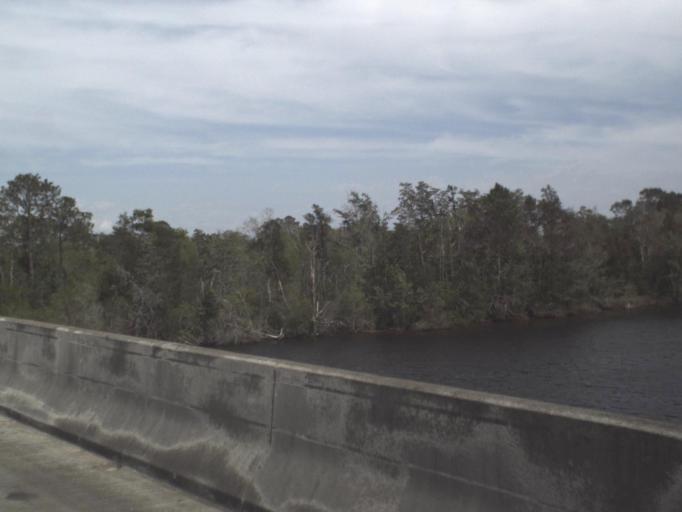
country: US
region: Florida
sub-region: Santa Rosa County
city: Milton
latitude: 30.6237
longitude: -87.0355
